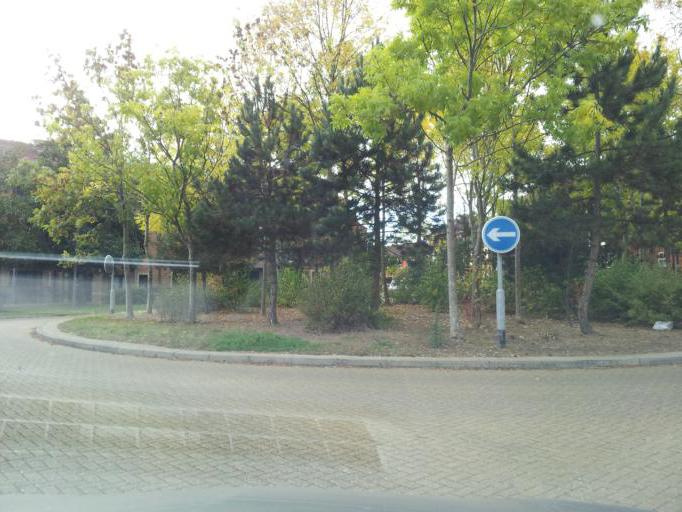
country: GB
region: England
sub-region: Milton Keynes
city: Shenley Church End
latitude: 52.0033
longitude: -0.7962
